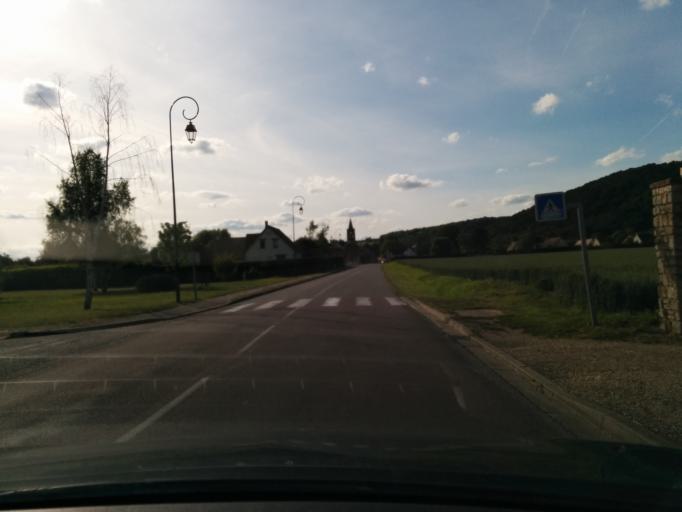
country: FR
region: Haute-Normandie
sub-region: Departement de l'Eure
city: Courcelles-sur-Seine
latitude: 49.1670
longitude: 1.4102
